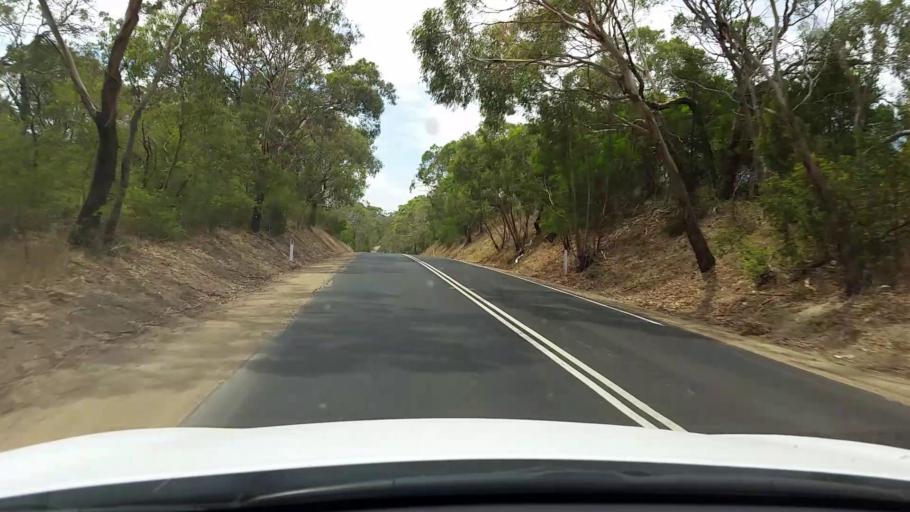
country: AU
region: Victoria
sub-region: Mornington Peninsula
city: Mount Martha
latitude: -38.2994
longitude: 145.0436
